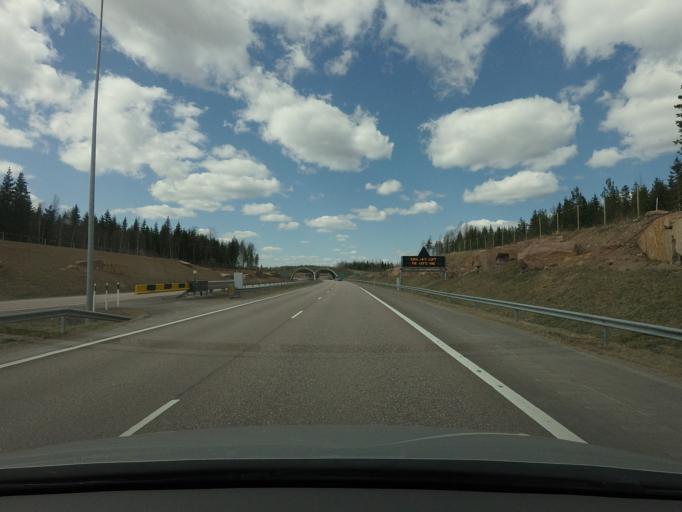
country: FI
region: Kymenlaakso
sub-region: Kotka-Hamina
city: Broby
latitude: 60.5008
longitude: 26.8119
